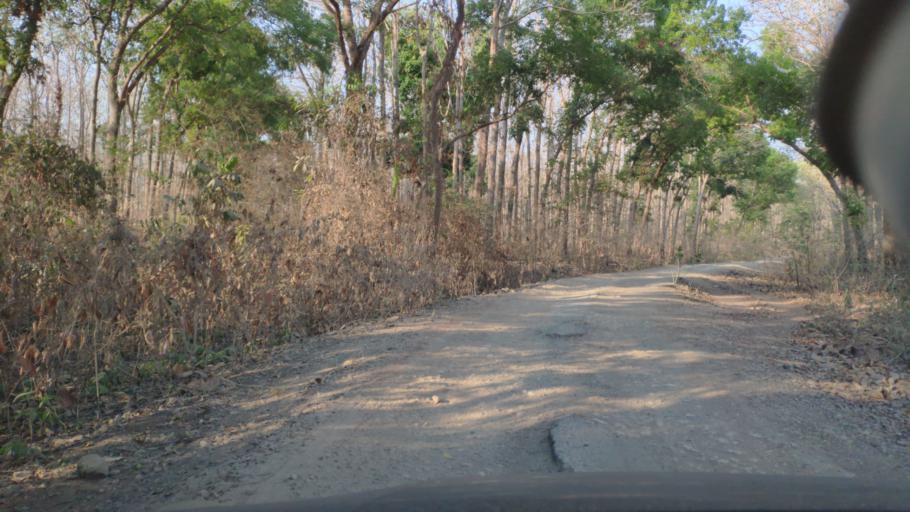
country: ID
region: Central Java
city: Sendangrejo
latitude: -6.9192
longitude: 111.5507
